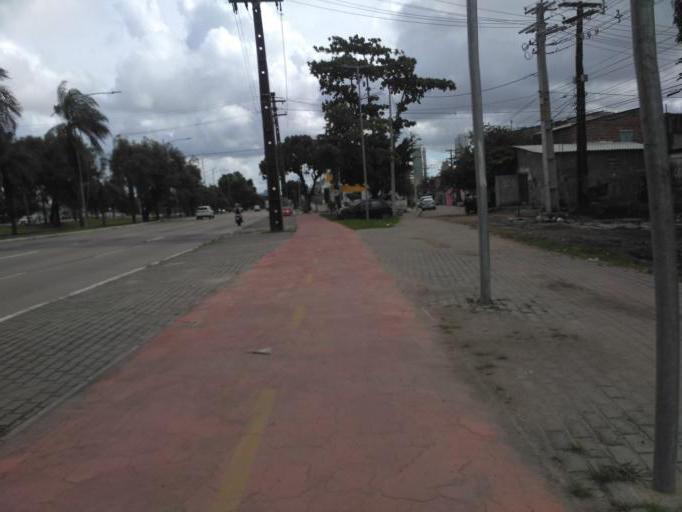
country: BR
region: Pernambuco
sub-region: Recife
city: Recife
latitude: -8.0369
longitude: -34.8735
